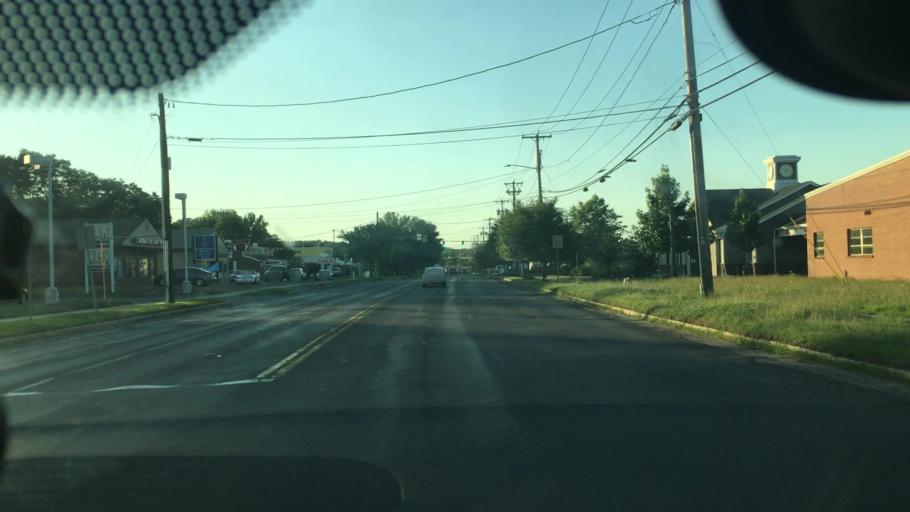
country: US
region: Massachusetts
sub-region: Hampshire County
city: Northampton
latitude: 42.3336
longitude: -72.6355
